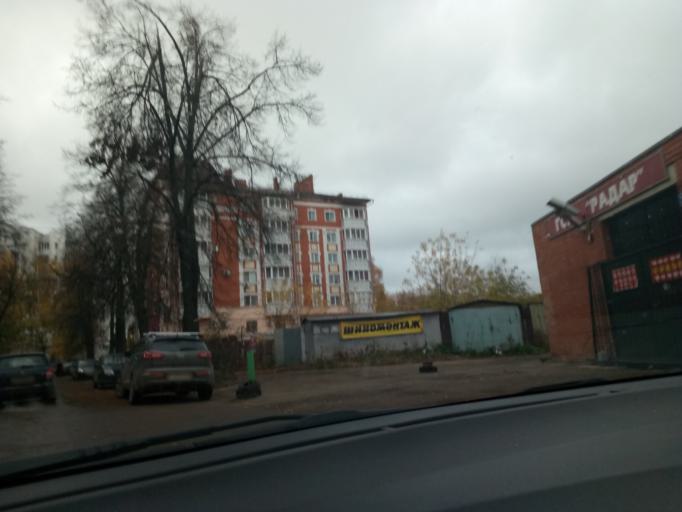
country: RU
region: Tatarstan
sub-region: Gorod Kazan'
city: Kazan
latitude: 55.7855
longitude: 49.1484
